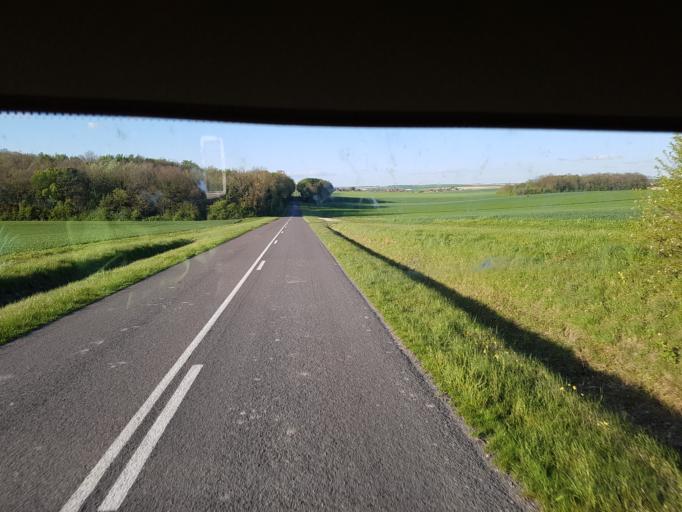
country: FR
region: Champagne-Ardenne
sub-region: Departement de l'Aube
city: Marigny-le-Chatel
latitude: 48.3734
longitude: 3.6410
